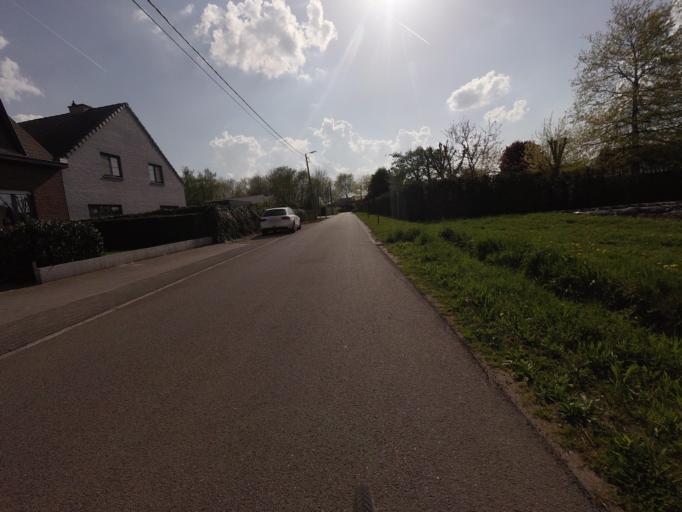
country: BE
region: Flanders
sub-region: Provincie Antwerpen
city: Putte
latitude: 51.0742
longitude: 4.6573
